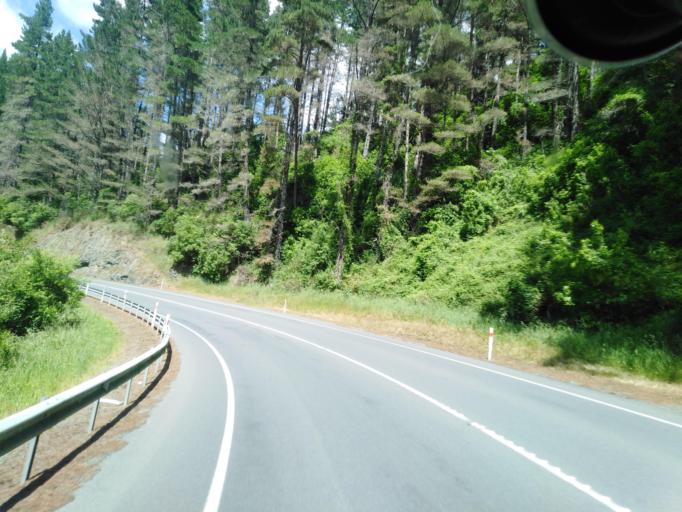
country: NZ
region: Nelson
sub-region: Nelson City
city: Nelson
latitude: -41.2281
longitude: 173.4016
